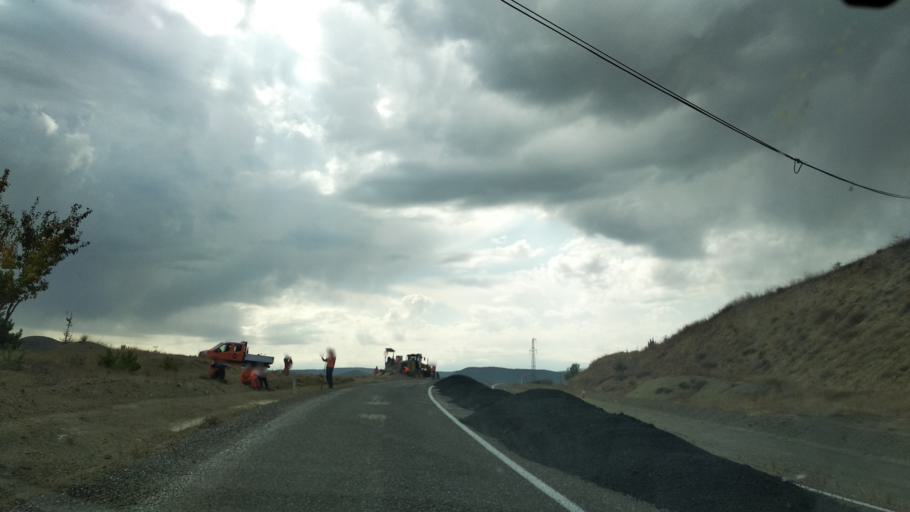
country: TR
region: Bolu
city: Seben
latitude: 40.3547
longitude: 31.4833
